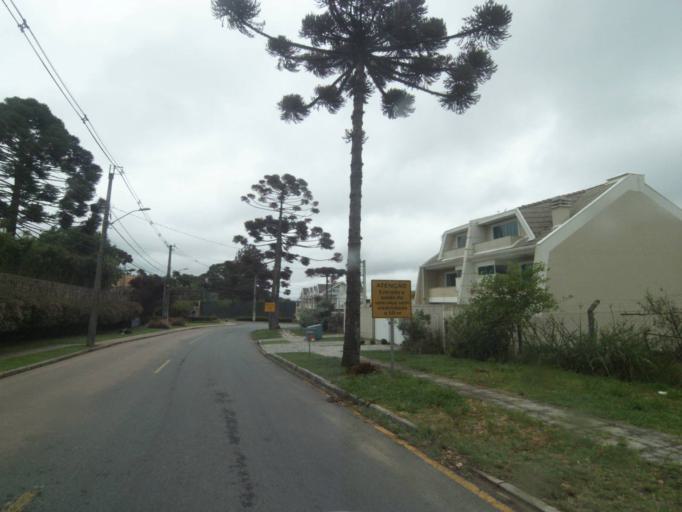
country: BR
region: Parana
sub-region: Curitiba
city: Curitiba
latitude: -25.4214
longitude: -49.3255
